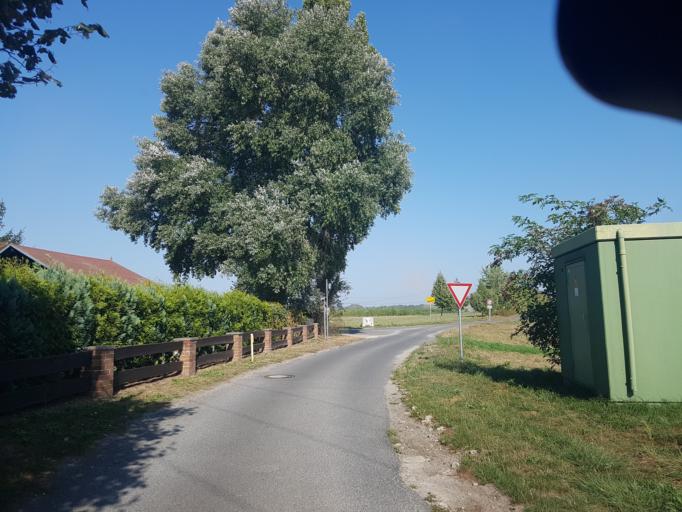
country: DE
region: Brandenburg
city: Finsterwalde
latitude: 51.6477
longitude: 13.7238
